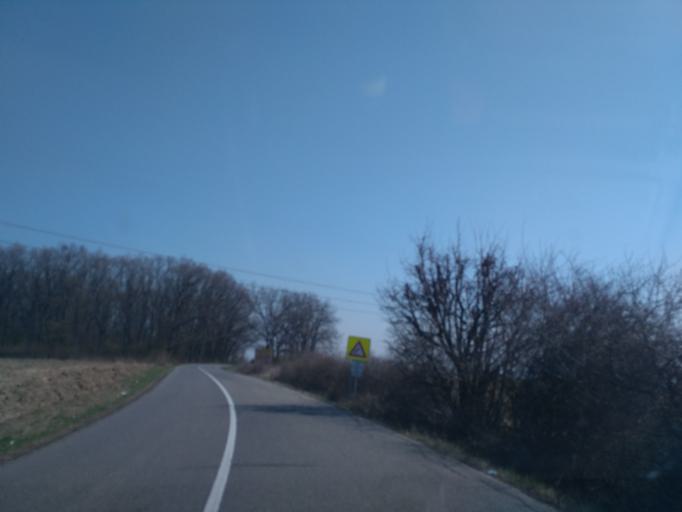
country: SK
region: Kosicky
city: Secovce
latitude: 48.7322
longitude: 21.5954
